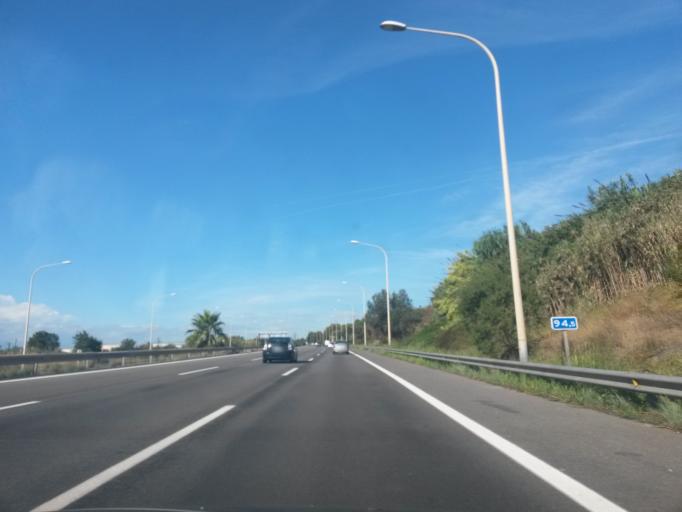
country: ES
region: Catalonia
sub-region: Provincia de Barcelona
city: Vilassar de Mar
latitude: 41.5174
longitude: 2.3906
